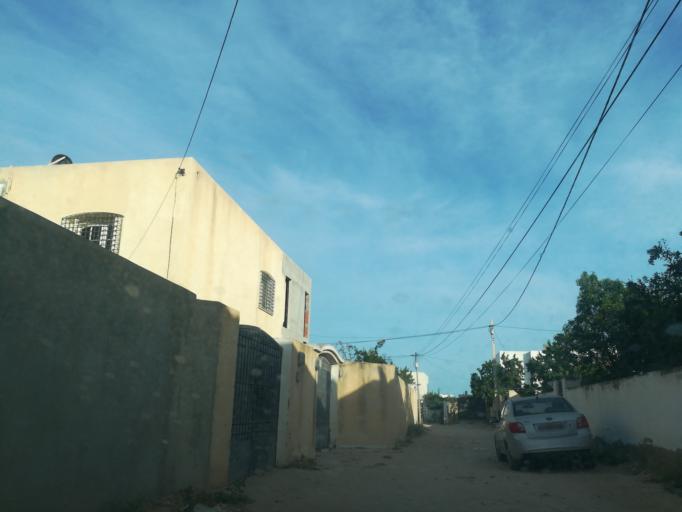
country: TN
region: Safaqis
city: Al Qarmadah
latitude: 34.8126
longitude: 10.7502
